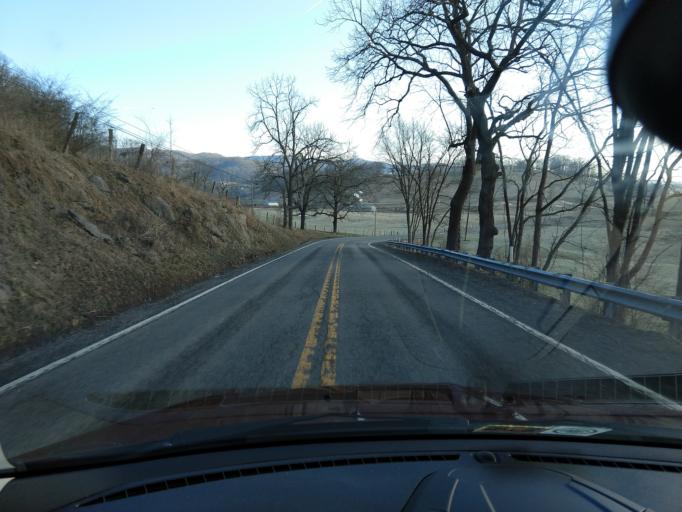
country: US
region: West Virginia
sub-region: Pocahontas County
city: Marlinton
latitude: 38.1239
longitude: -80.2368
